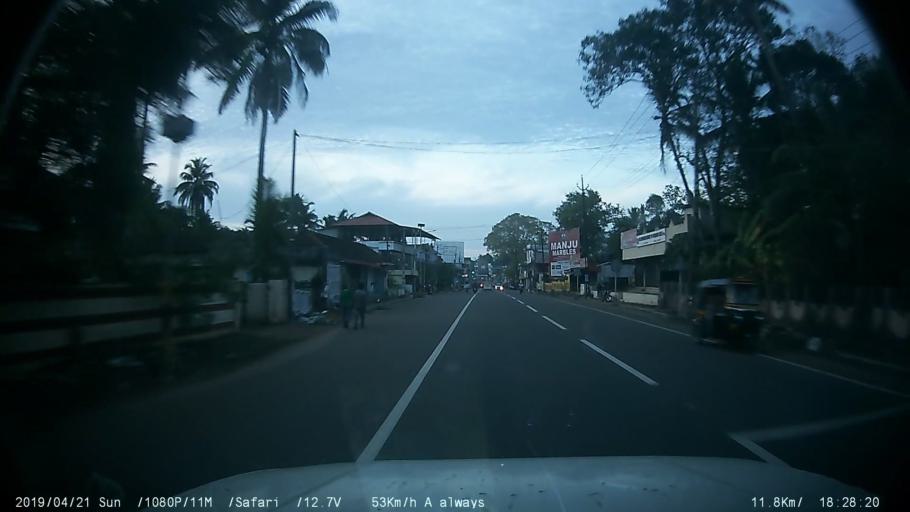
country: IN
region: Kerala
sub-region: Kottayam
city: Changanacheri
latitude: 9.4977
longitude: 76.5254
